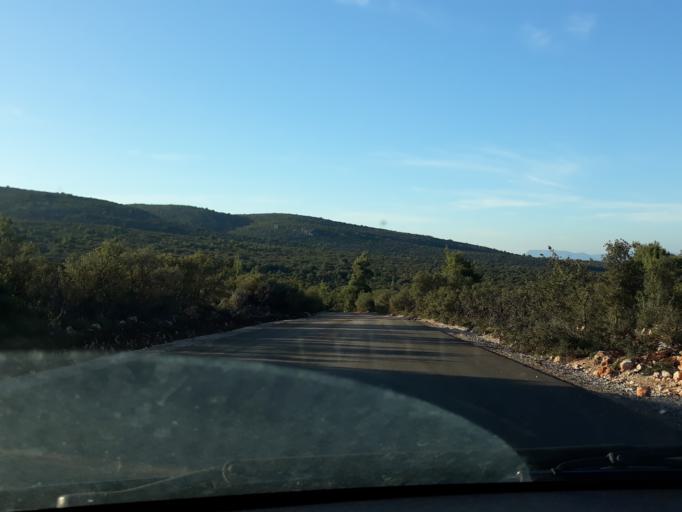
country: GR
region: Central Greece
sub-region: Nomos Voiotias
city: Ayios Thomas
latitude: 38.2353
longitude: 23.5346
